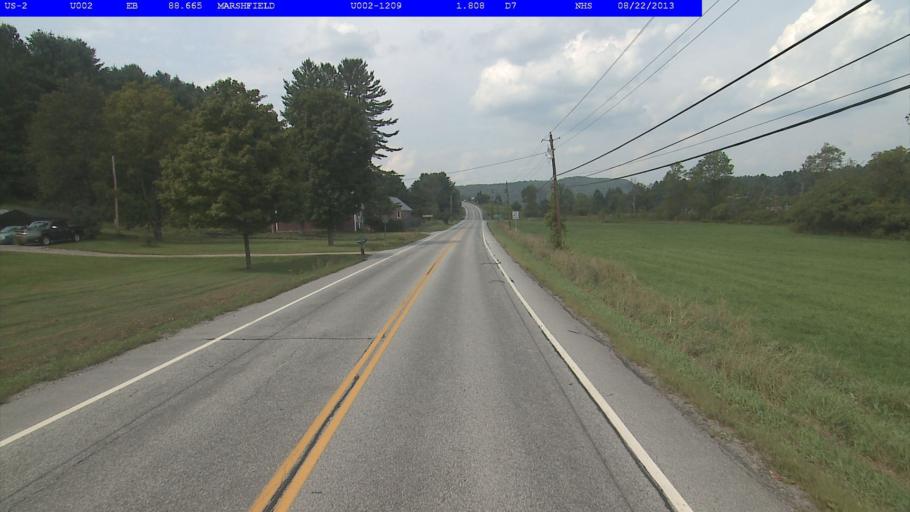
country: US
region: Vermont
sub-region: Washington County
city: Barre
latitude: 44.2970
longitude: -72.3983
